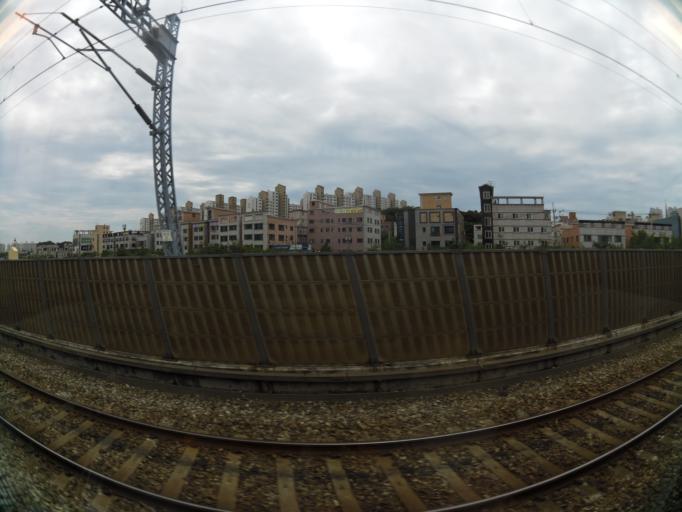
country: KR
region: Gyeonggi-do
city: Osan
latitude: 37.1750
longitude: 127.0599
